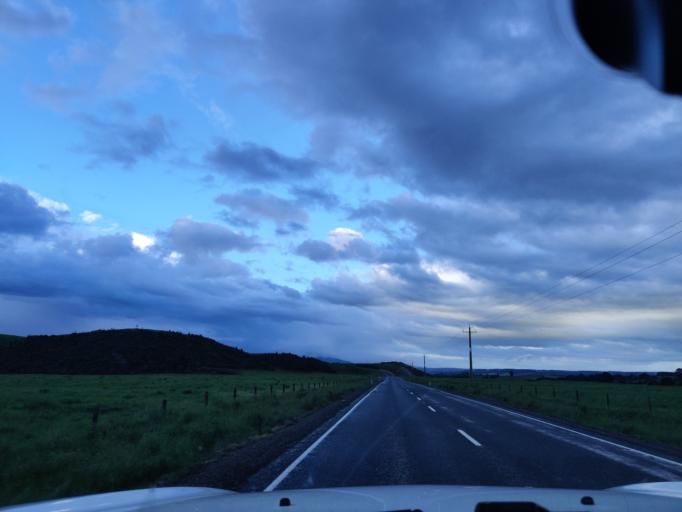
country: NZ
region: Waikato
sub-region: South Waikato District
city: Tokoroa
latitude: -38.3797
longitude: 175.7877
